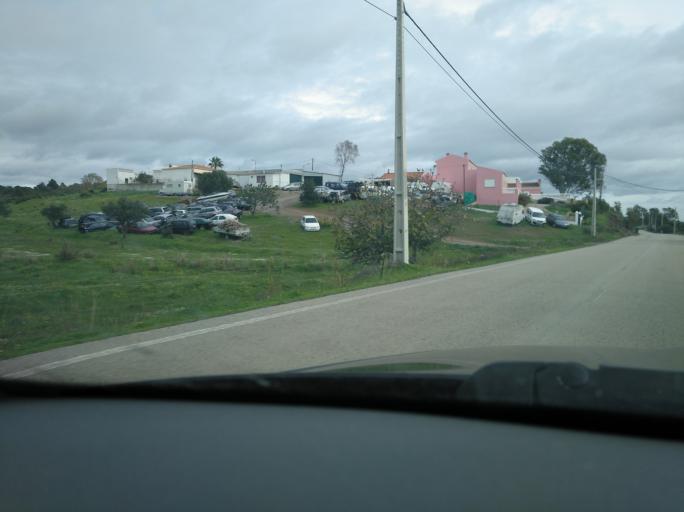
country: PT
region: Faro
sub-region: Castro Marim
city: Castro Marim
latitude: 37.2188
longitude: -7.4664
